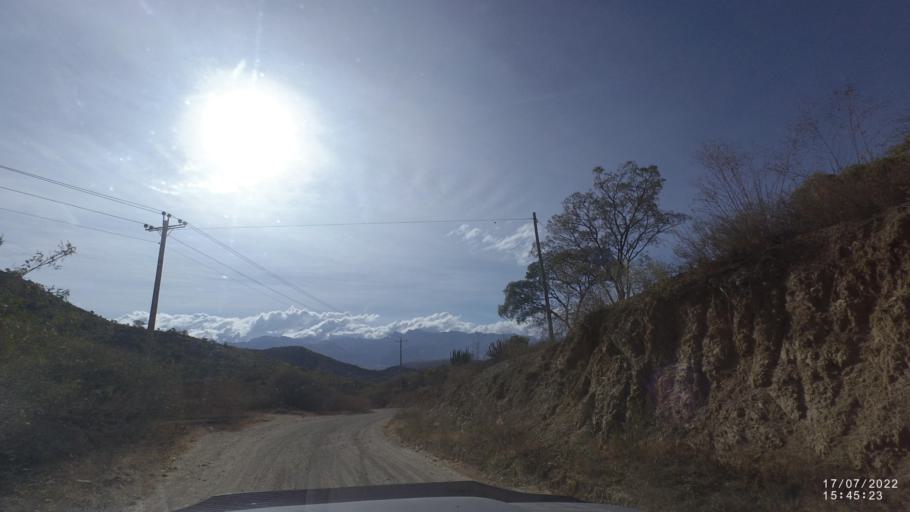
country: BO
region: Cochabamba
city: Sipe Sipe
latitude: -17.4708
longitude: -66.2847
